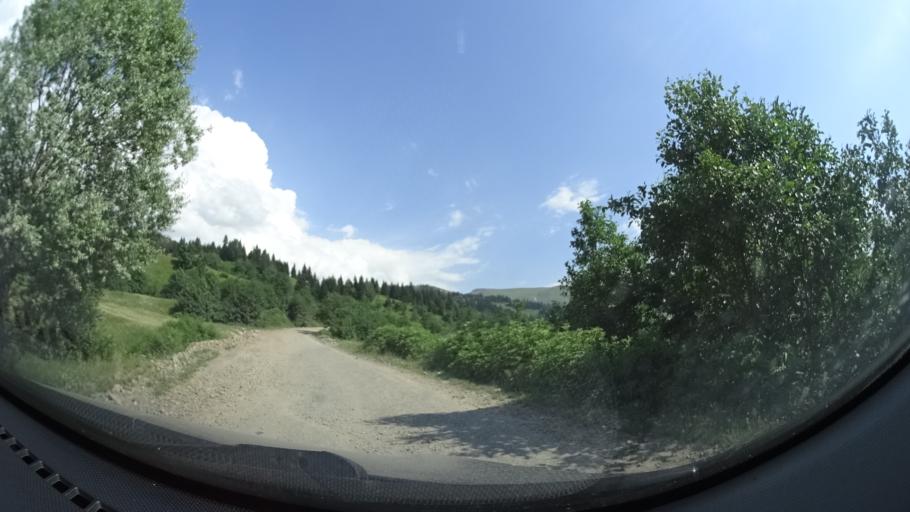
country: GE
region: Ajaria
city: Dioknisi
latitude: 41.6437
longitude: 42.4916
